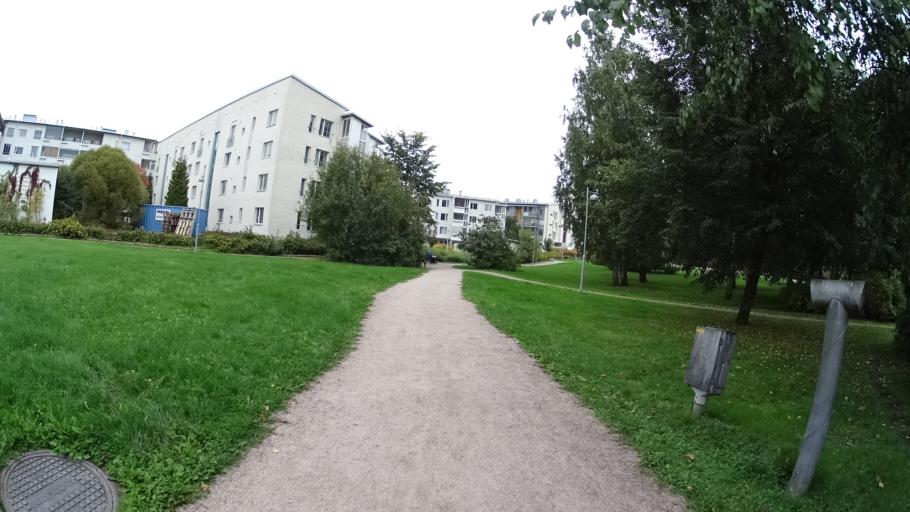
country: FI
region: Uusimaa
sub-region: Helsinki
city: Helsinki
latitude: 60.1972
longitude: 24.9683
